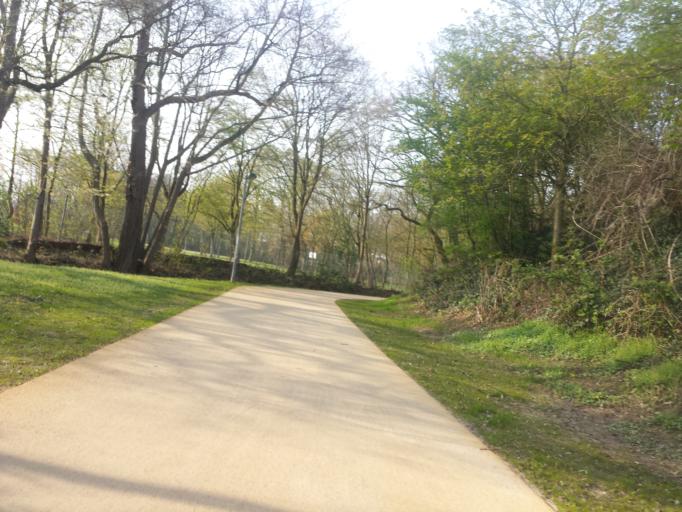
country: DE
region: Lower Saxony
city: Lilienthal
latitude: 53.0642
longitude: 8.9026
